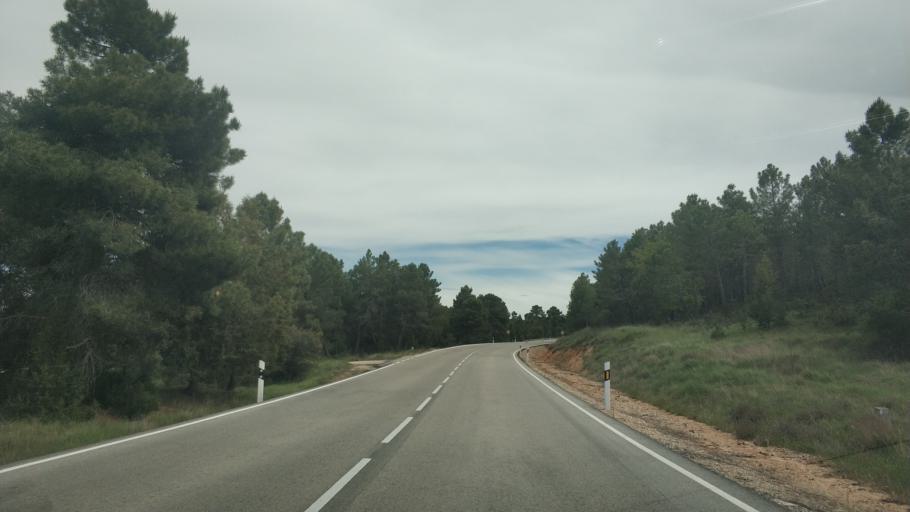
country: ES
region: Castille and Leon
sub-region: Provincia de Soria
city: Valdenebro
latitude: 41.5545
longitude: -2.9645
